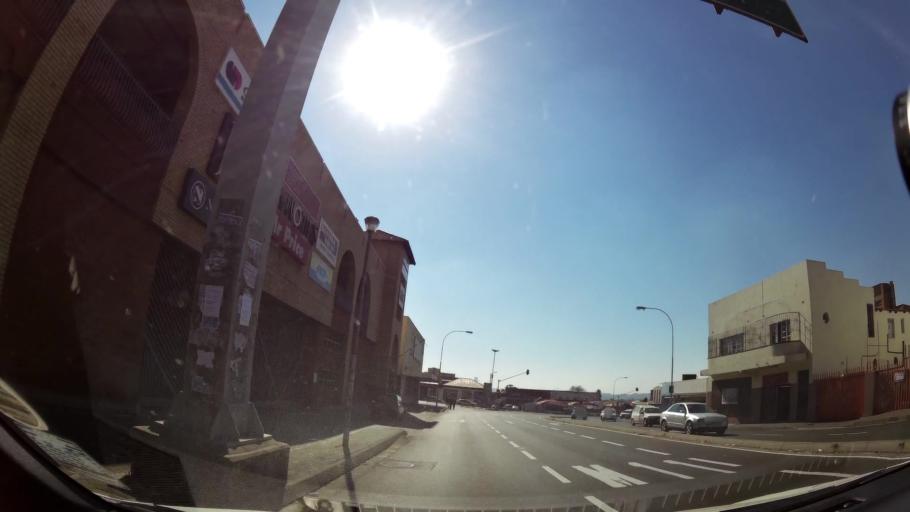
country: ZA
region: Gauteng
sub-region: City of Johannesburg Metropolitan Municipality
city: Johannesburg
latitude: -26.2443
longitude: 28.0552
